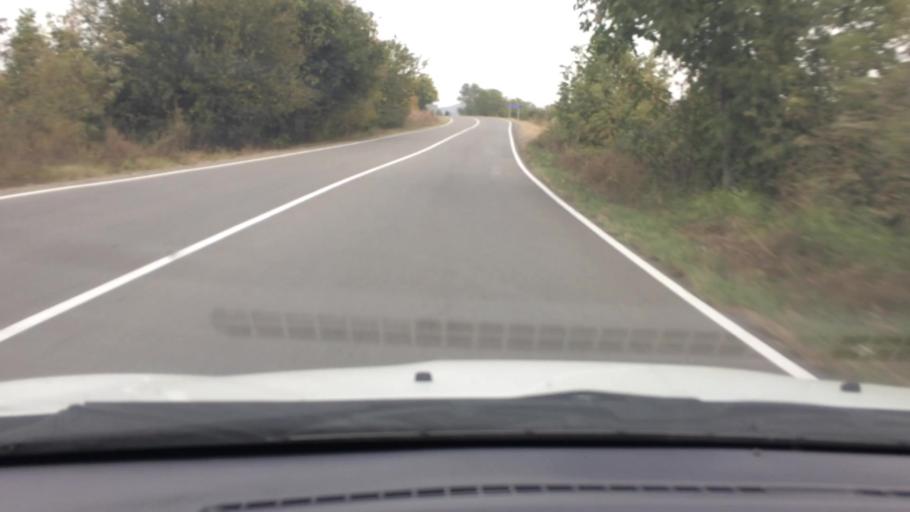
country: GE
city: Naghvarevi
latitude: 41.3293
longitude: 44.8030
